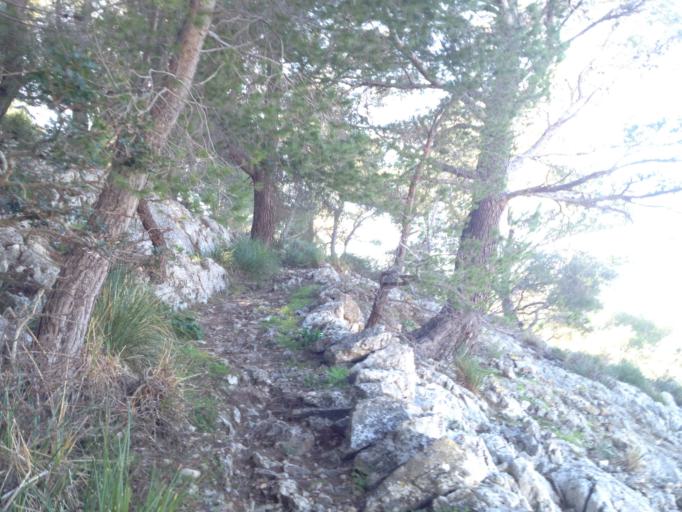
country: ES
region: Balearic Islands
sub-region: Illes Balears
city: Pollenca
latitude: 39.8691
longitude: 3.0211
